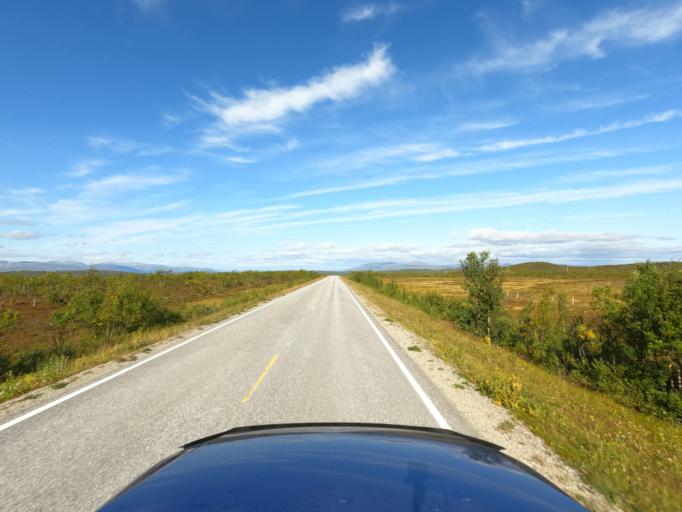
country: NO
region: Finnmark Fylke
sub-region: Karasjok
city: Karasjohka
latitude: 69.7197
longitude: 25.2378
